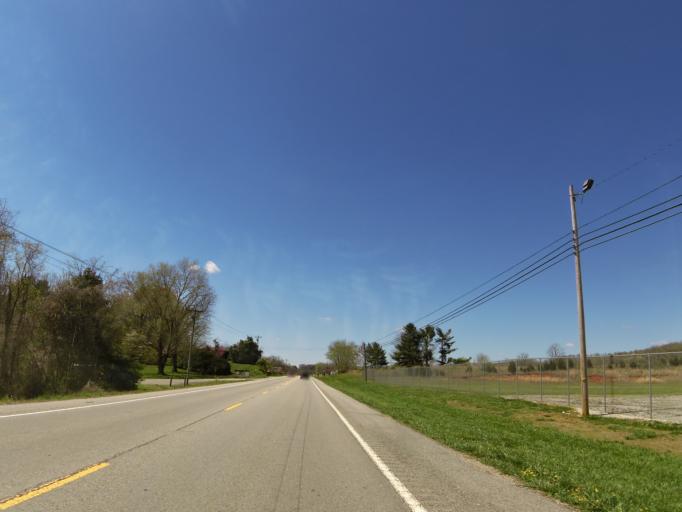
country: US
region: Tennessee
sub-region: White County
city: Sparta
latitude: 35.9447
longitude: -85.5168
